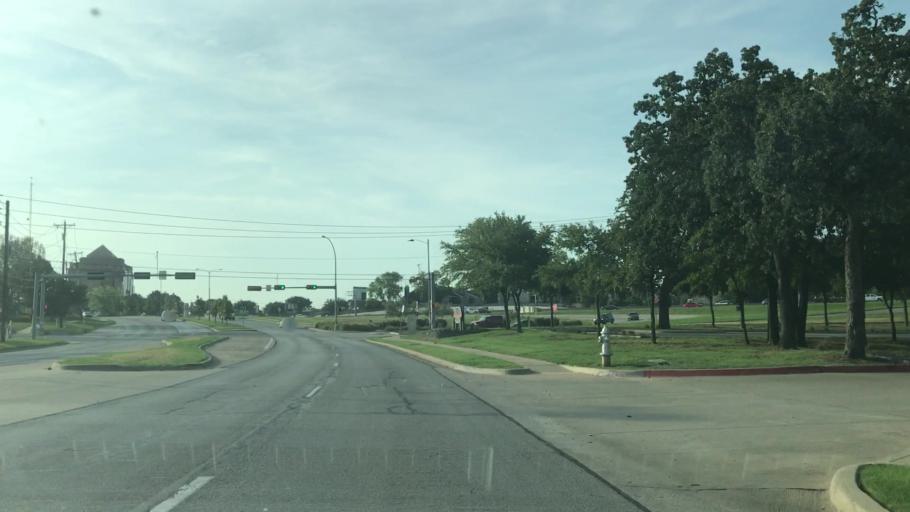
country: US
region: Texas
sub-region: Tarrant County
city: Arlington
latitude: 32.7618
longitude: -97.1192
